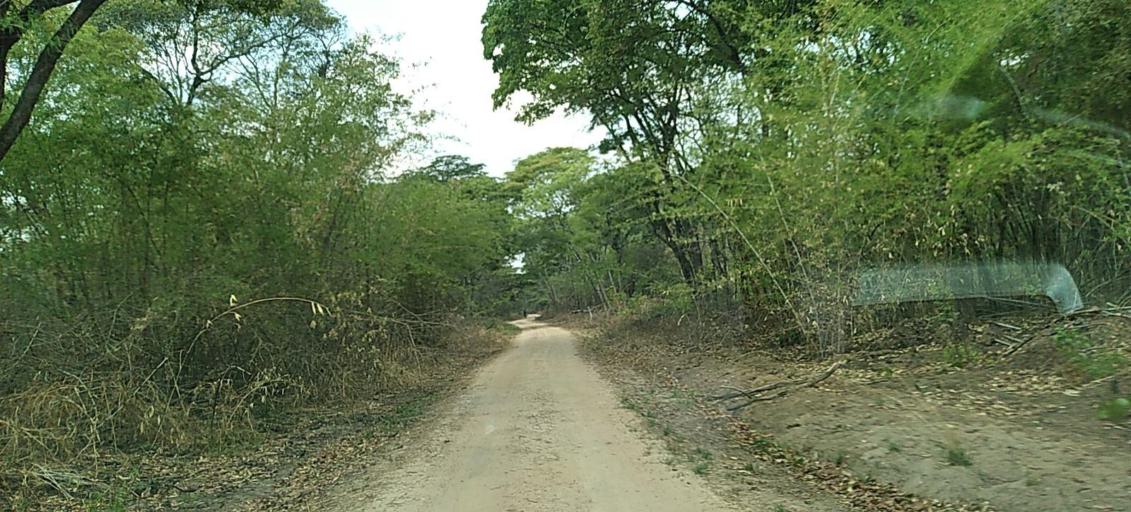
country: ZM
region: Copperbelt
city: Chingola
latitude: -12.7544
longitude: 27.7112
